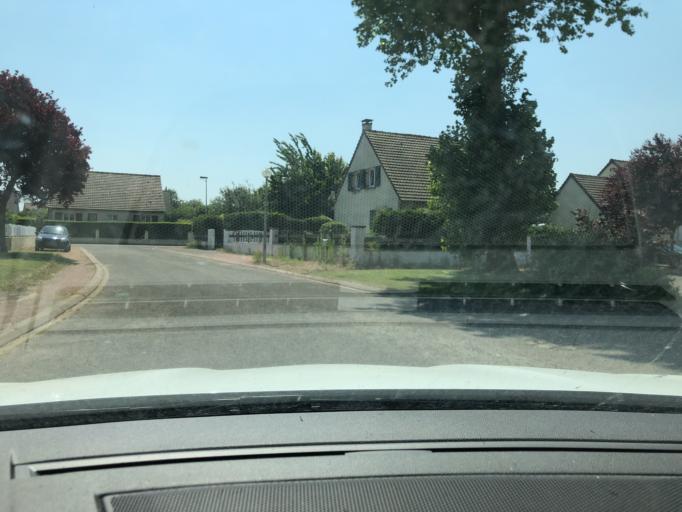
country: FR
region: Lower Normandy
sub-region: Departement du Calvados
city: Lion-sur-Mer
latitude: 49.3028
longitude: -0.3251
